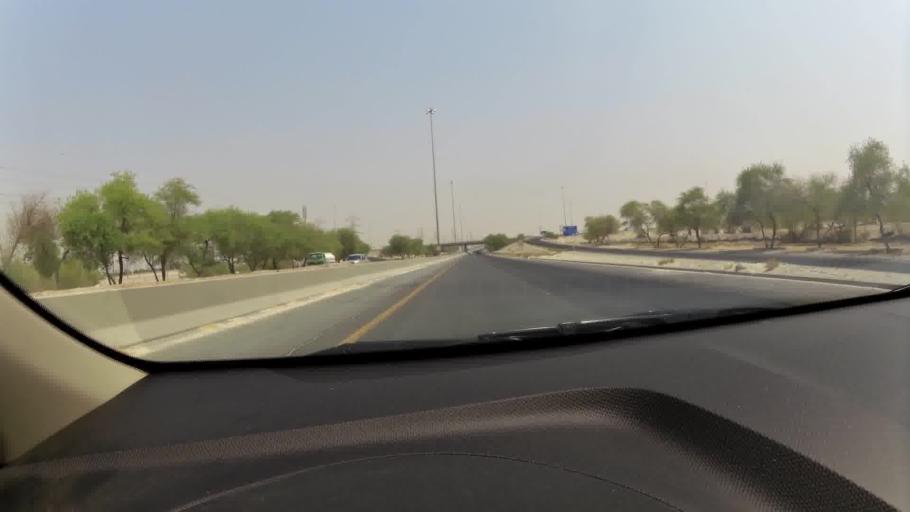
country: KW
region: Al Asimah
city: Ar Rabiyah
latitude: 29.2562
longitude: 47.8570
